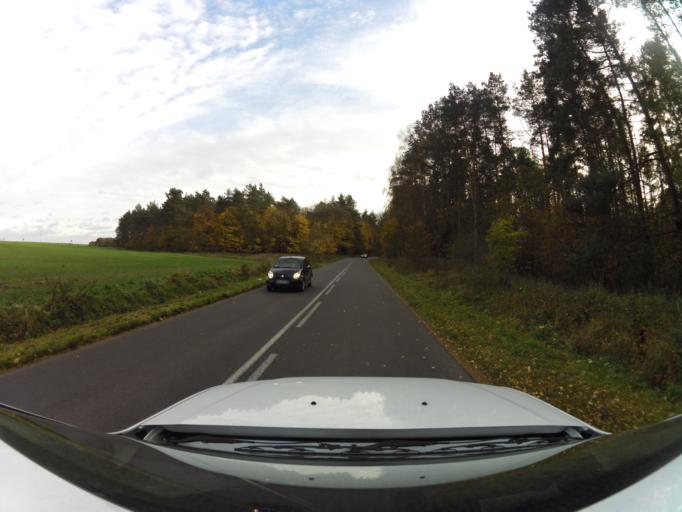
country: PL
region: West Pomeranian Voivodeship
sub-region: Powiat gryficki
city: Gryfice
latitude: 53.8633
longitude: 15.1152
